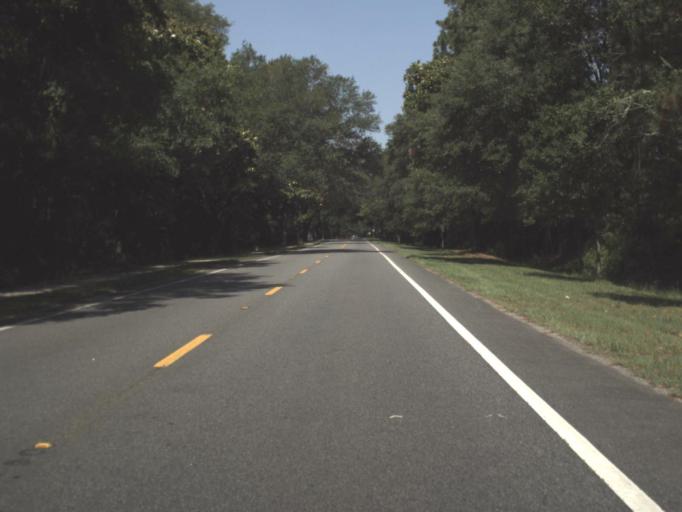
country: US
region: Florida
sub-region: Clay County
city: Asbury Lake
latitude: 29.9824
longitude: -81.8167
